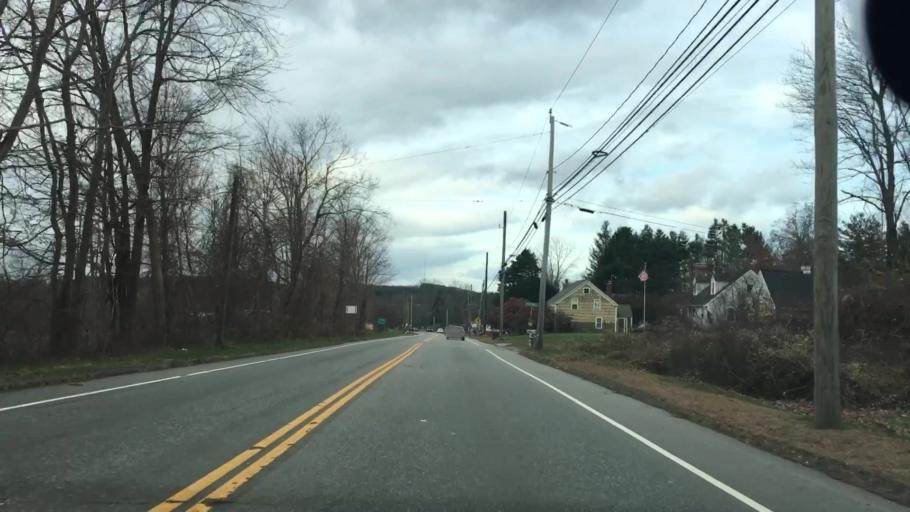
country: US
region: Connecticut
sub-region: Tolland County
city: Rockville
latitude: 41.7969
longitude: -72.4156
